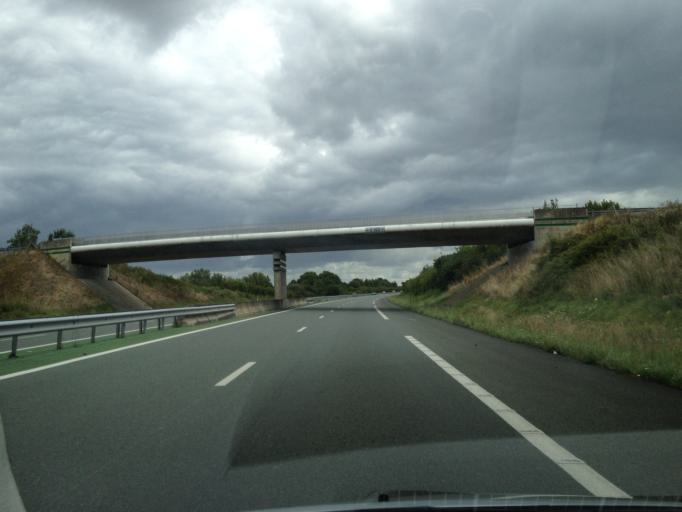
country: FR
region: Pays de la Loire
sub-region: Departement de la Vendee
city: Beaurepaire
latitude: 46.8925
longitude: -1.0929
